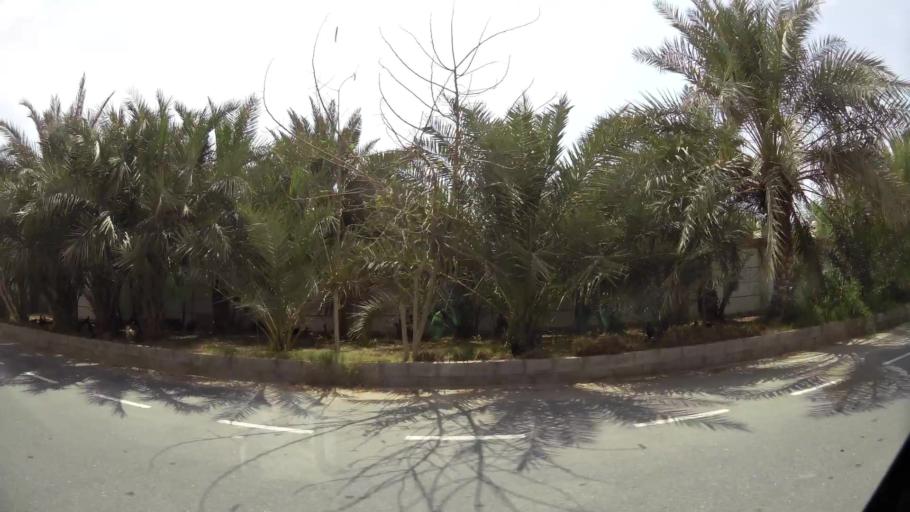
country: AE
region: Ash Shariqah
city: Sharjah
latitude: 25.2401
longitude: 55.4357
